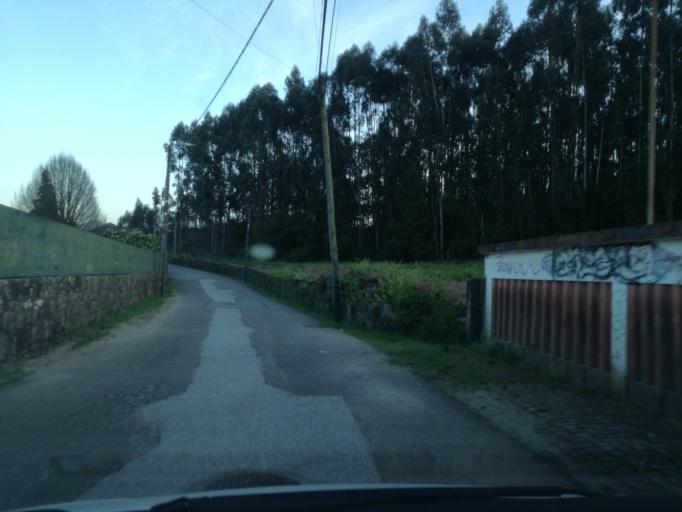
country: PT
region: Porto
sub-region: Maia
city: Anta
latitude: 41.2716
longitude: -8.6214
